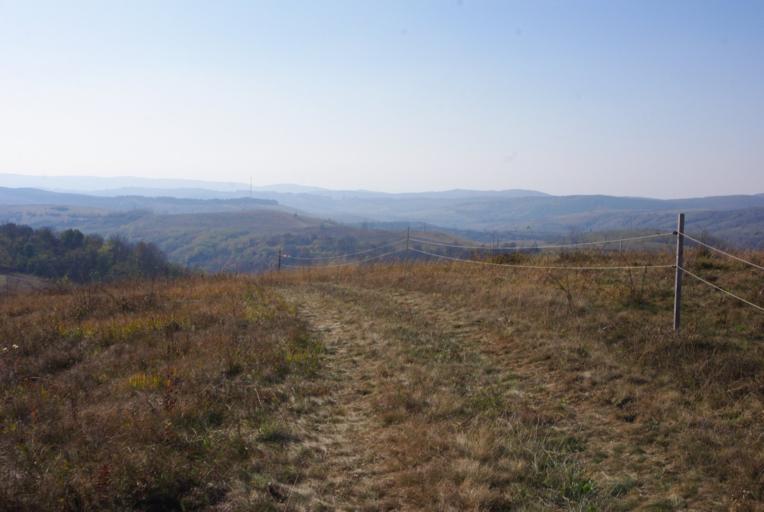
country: HU
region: Borsod-Abauj-Zemplen
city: Borsodnadasd
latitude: 48.0610
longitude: 20.2733
